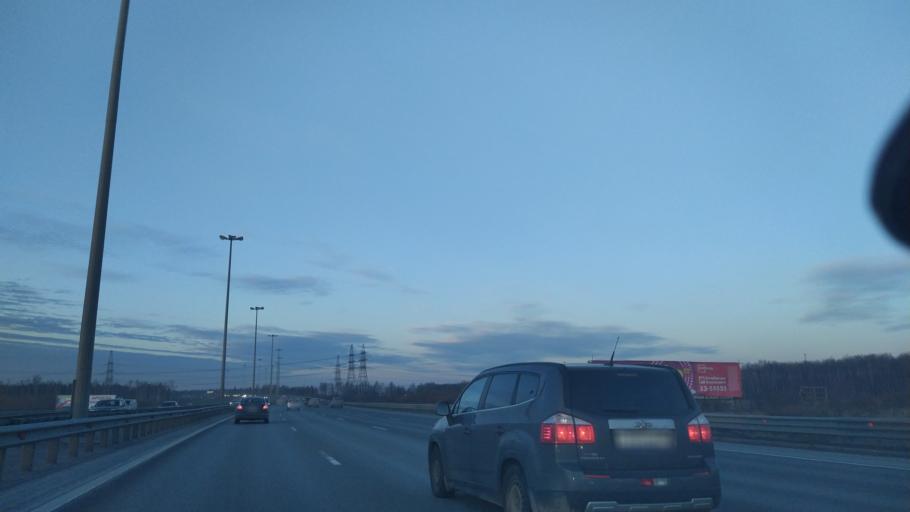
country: RU
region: St.-Petersburg
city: Krasnogvargeisky
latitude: 59.9247
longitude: 30.5297
